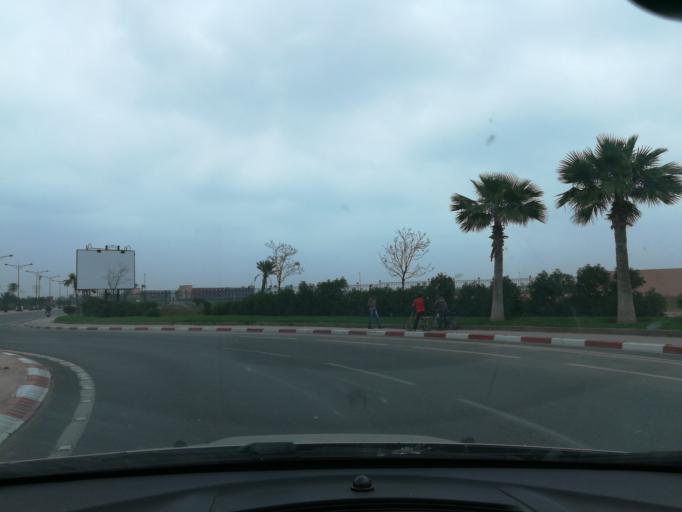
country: MA
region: Marrakech-Tensift-Al Haouz
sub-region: Marrakech
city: Marrakesh
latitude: 31.6804
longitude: -7.9973
